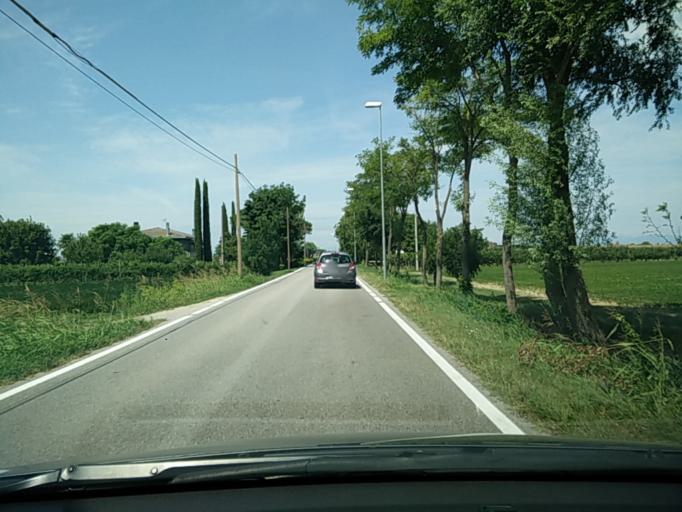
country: IT
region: Veneto
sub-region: Provincia di Venezia
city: Passarella
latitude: 45.5733
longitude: 12.6177
